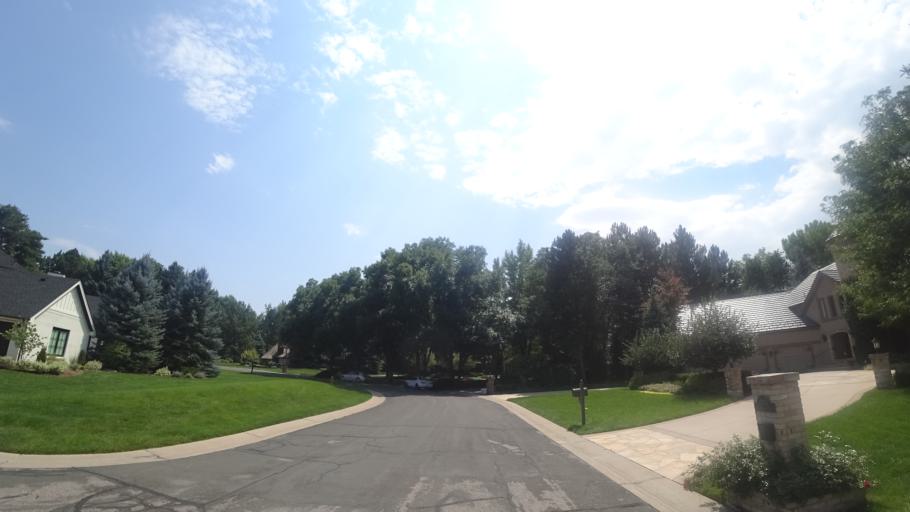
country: US
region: Colorado
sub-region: Arapahoe County
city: Greenwood Village
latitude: 39.6200
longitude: -104.9733
